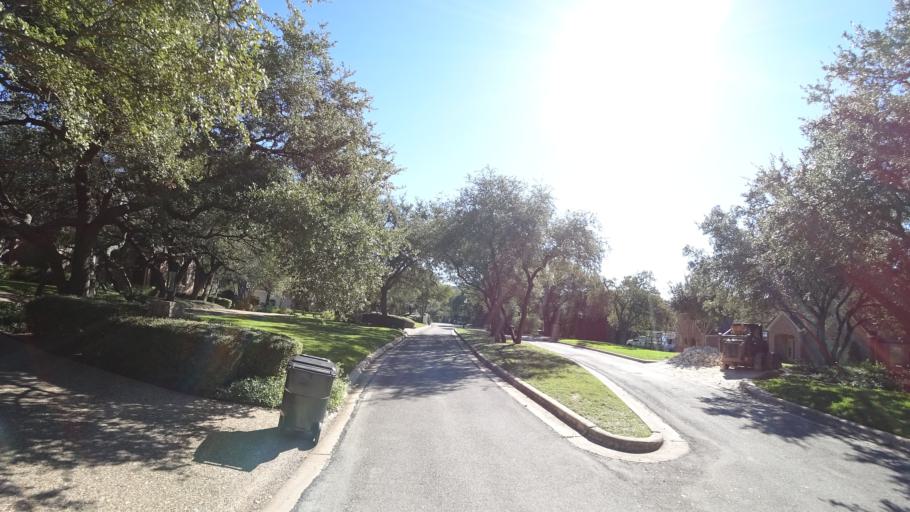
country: US
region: Texas
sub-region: Travis County
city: West Lake Hills
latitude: 30.3318
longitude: -97.7861
